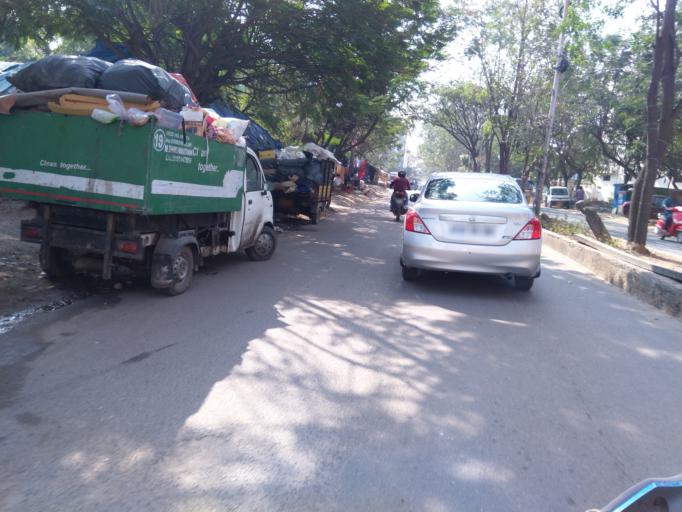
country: IN
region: Telangana
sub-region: Rangareddi
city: Kukatpalli
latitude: 17.4826
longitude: 78.3936
